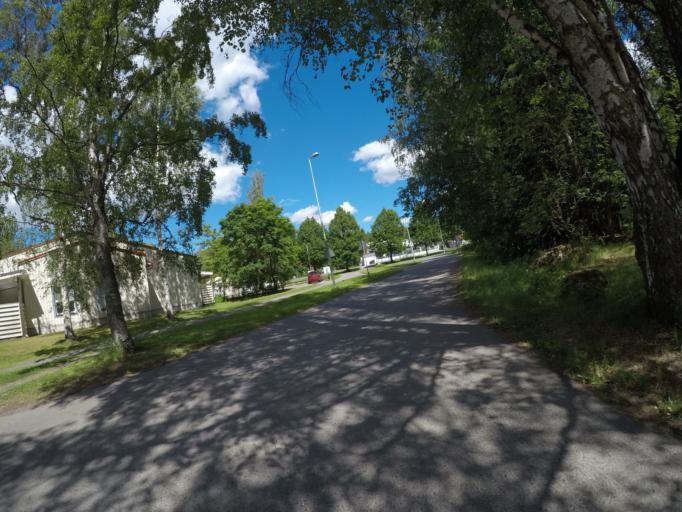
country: FI
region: Haeme
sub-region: Haemeenlinna
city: Haemeenlinna
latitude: 61.0100
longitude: 24.4374
